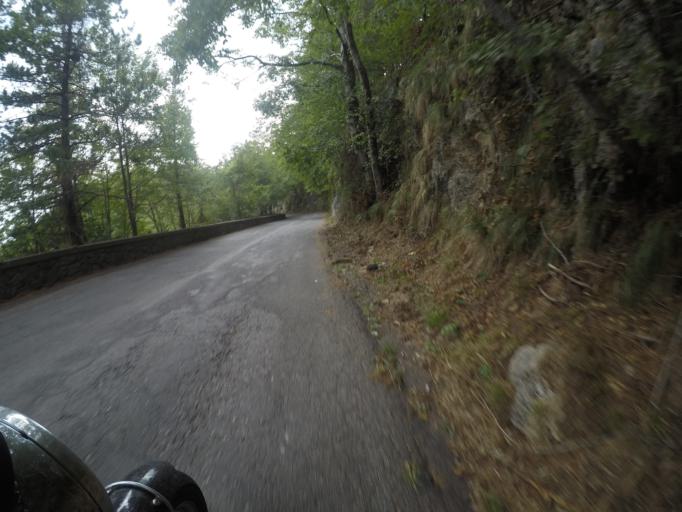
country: IT
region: Tuscany
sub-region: Provincia di Massa-Carrara
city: Carrara
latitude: 44.1199
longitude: 10.1061
